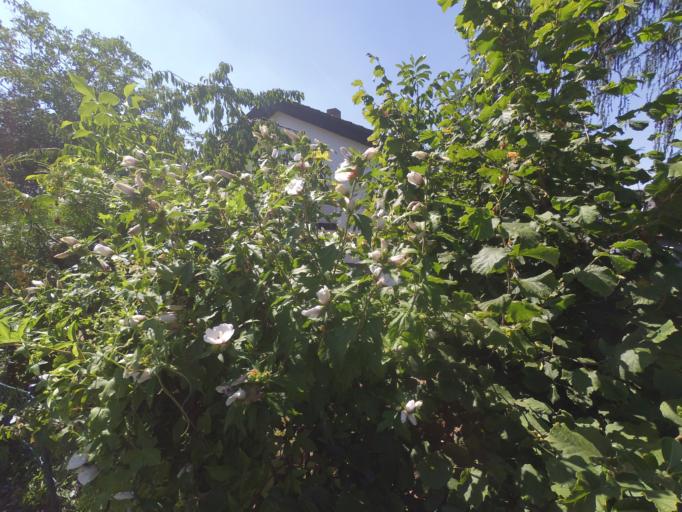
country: DE
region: Baden-Wuerttemberg
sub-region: Karlsruhe Region
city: Bruhl
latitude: 49.4028
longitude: 8.5332
